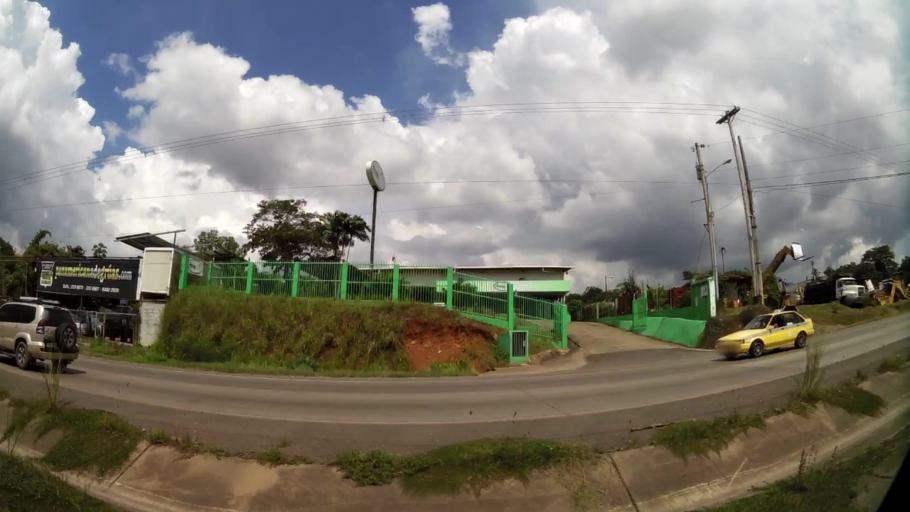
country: PA
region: Panama
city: Tocumen
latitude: 9.1028
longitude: -79.3825
